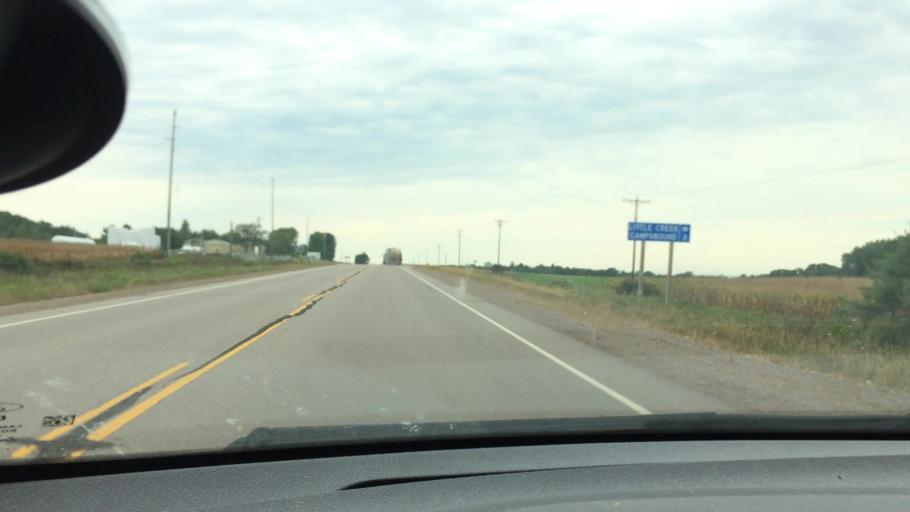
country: US
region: Wisconsin
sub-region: Eau Claire County
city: Augusta
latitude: 44.5964
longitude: -90.9303
